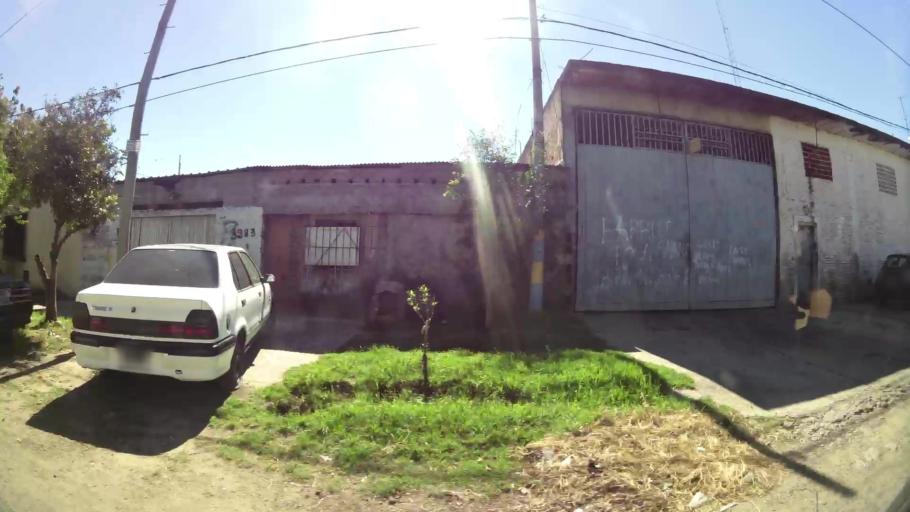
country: AR
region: Santa Fe
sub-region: Departamento de Rosario
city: Rosario
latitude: -32.9669
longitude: -60.6962
